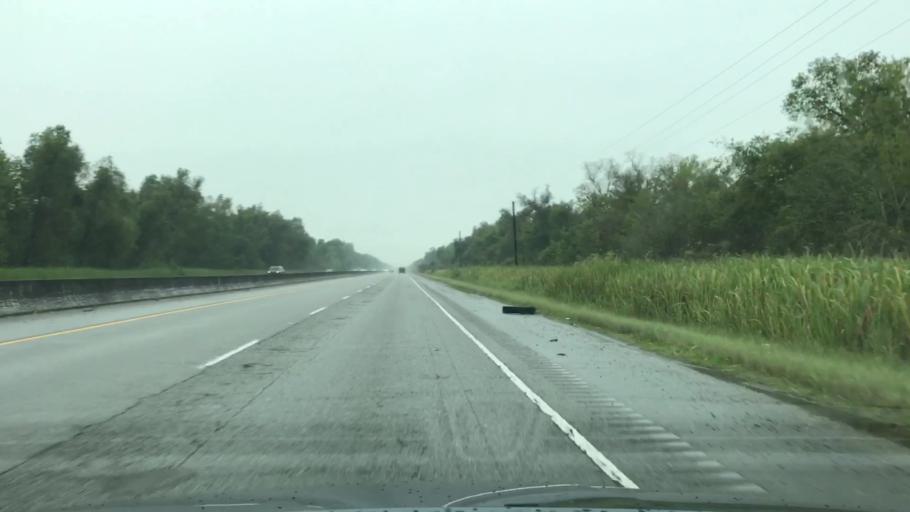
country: US
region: Louisiana
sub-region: Saint Charles Parish
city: Des Allemands
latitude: 29.7785
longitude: -90.5287
